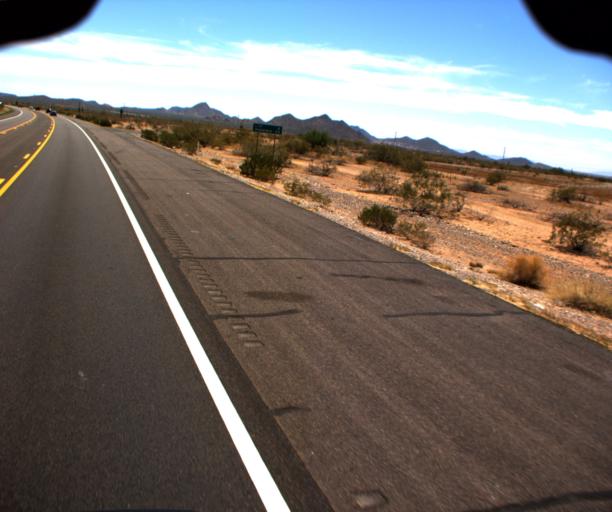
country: US
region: Arizona
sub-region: Maricopa County
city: Anthem
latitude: 33.8024
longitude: -112.2388
